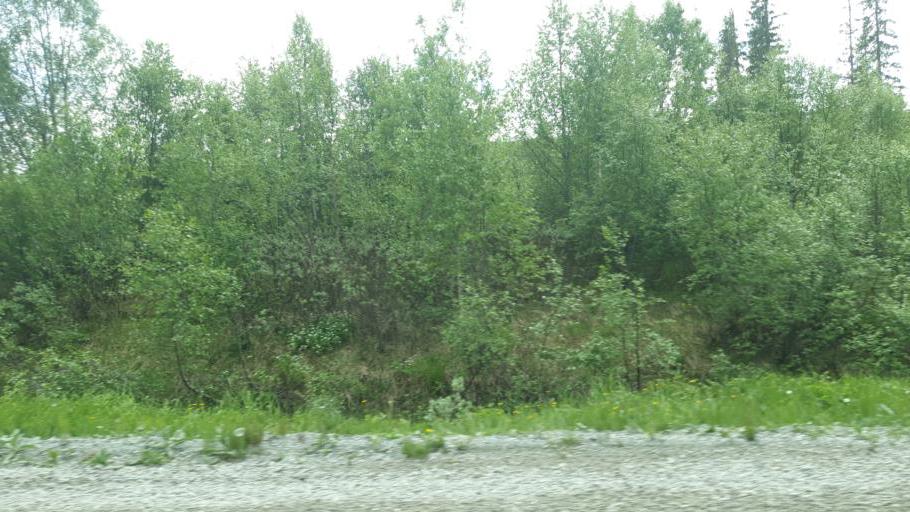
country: NO
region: Nord-Trondelag
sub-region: Leksvik
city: Leksvik
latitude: 63.6855
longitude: 10.3820
